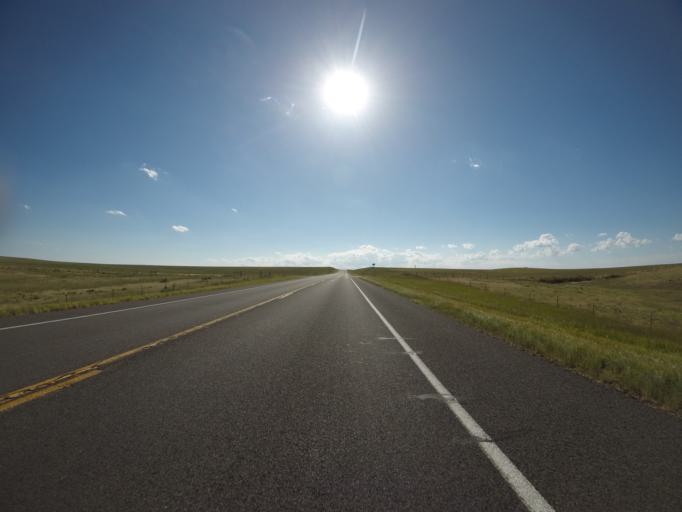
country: US
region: Colorado
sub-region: Logan County
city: Sterling
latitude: 40.6110
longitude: -103.5618
